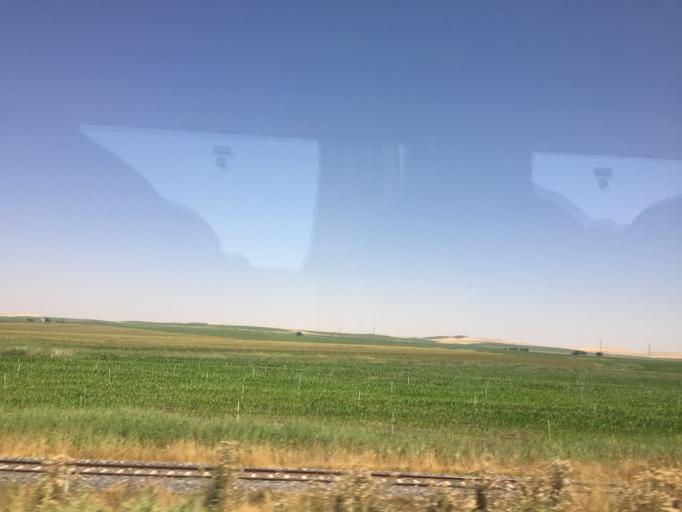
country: TR
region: Diyarbakir
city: Tepe
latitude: 37.8509
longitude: 40.7655
